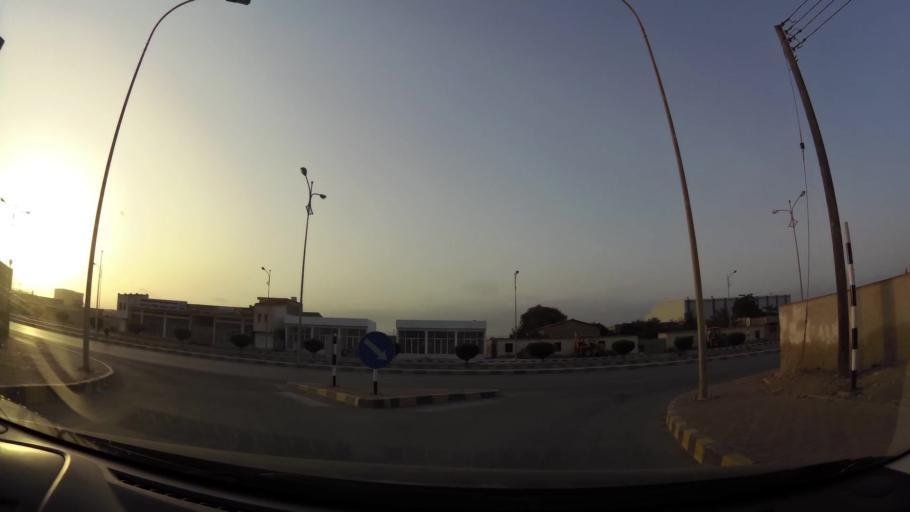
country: OM
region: Zufar
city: Salalah
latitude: 17.0206
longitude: 54.1185
